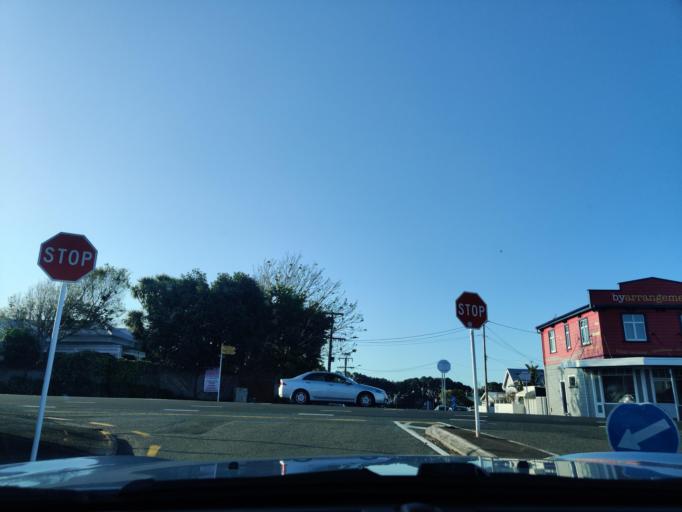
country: NZ
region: Taranaki
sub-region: New Plymouth District
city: New Plymouth
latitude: -39.0588
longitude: 174.0619
